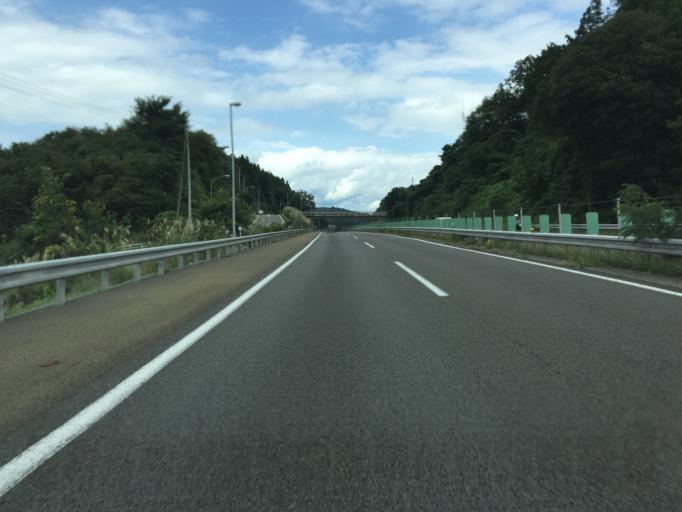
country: JP
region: Miyagi
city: Iwanuma
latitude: 38.1778
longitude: 140.7693
